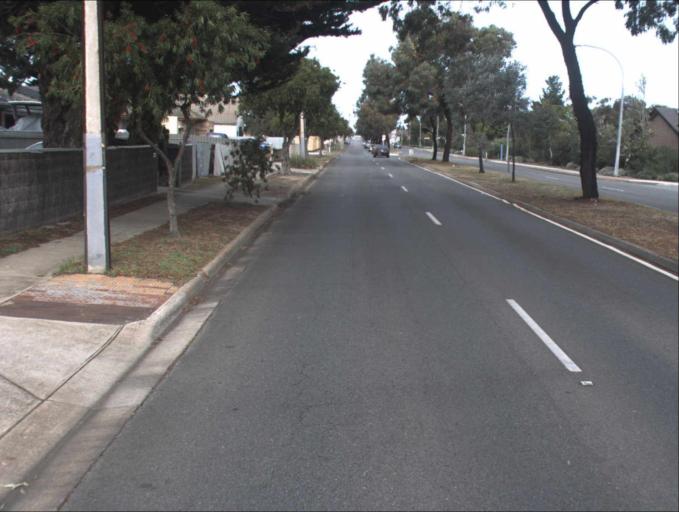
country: AU
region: South Australia
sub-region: Charles Sturt
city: Royal Park
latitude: -34.8733
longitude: 138.5036
